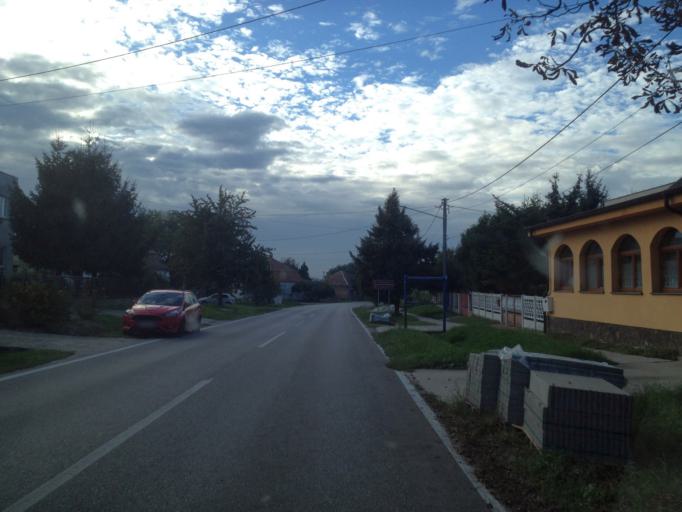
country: HU
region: Komarom-Esztergom
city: Almasfuzito
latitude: 47.7495
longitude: 18.2231
